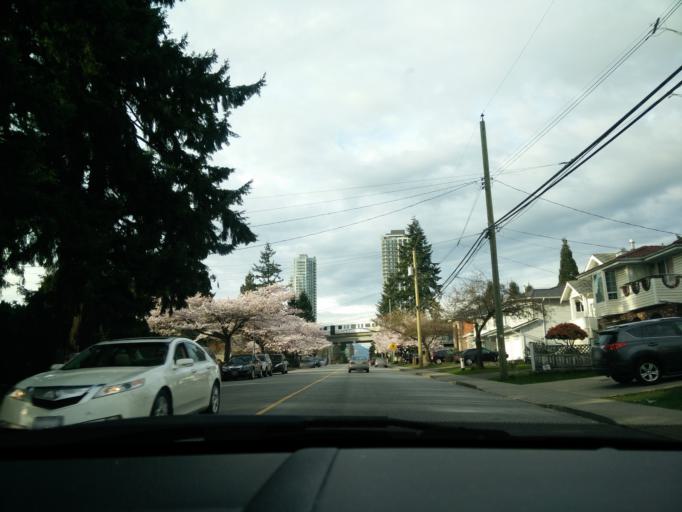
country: CA
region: British Columbia
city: Burnaby
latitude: 49.2200
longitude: -122.9941
